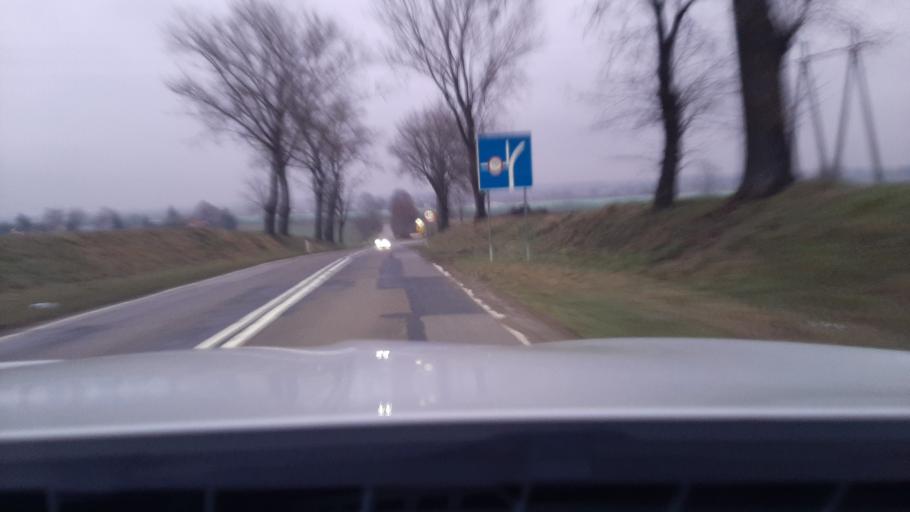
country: PL
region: Lublin Voivodeship
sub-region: Powiat lubelski
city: Garbow
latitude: 51.3469
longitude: 22.3651
